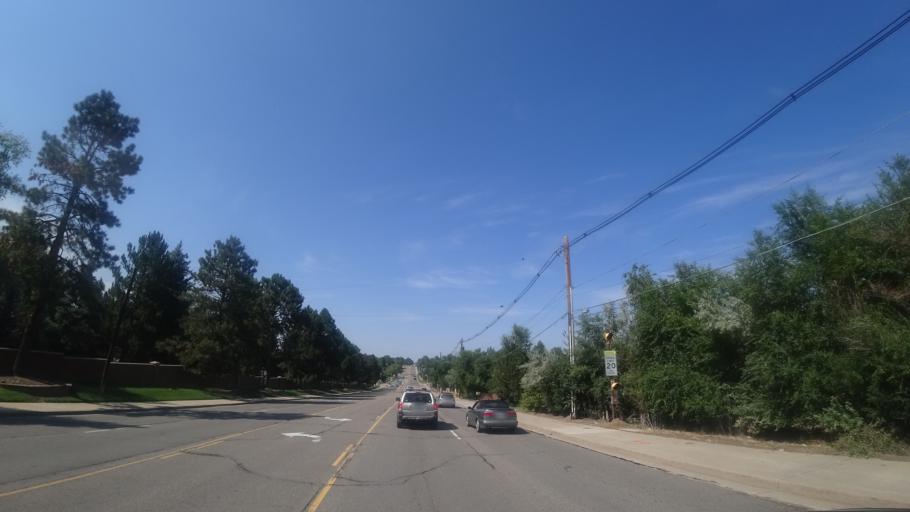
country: US
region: Colorado
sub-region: Arapahoe County
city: Cherry Hills Village
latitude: 39.6353
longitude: -104.9596
